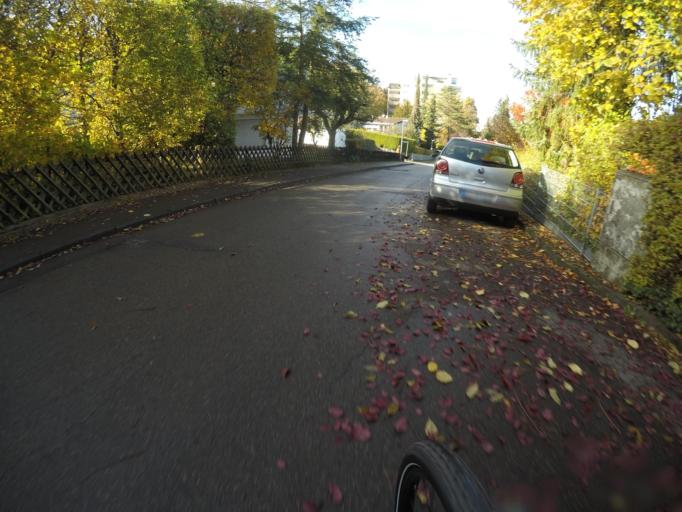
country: DE
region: Baden-Wuerttemberg
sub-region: Regierungsbezirk Stuttgart
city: Leinfelden-Echterdingen
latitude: 48.6827
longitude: 9.1509
